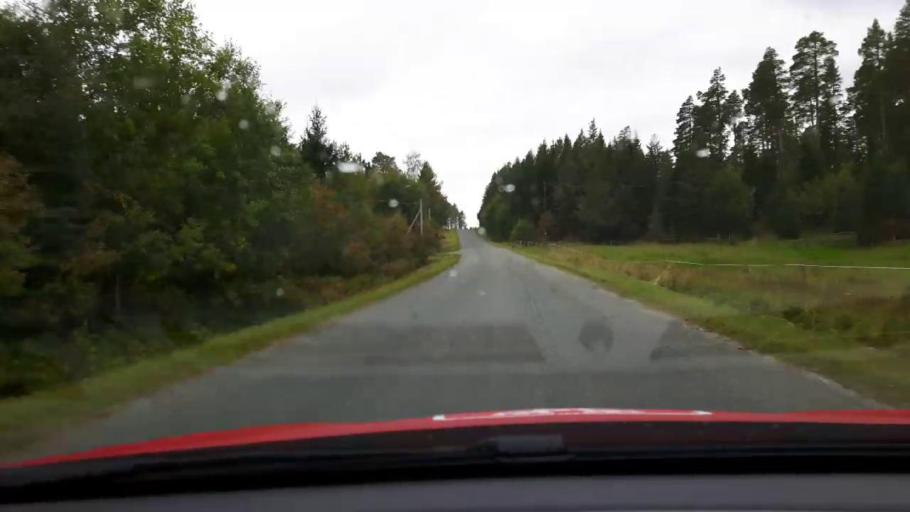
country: SE
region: Jaemtland
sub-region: Bergs Kommun
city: Hoverberg
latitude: 62.8567
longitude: 14.3232
